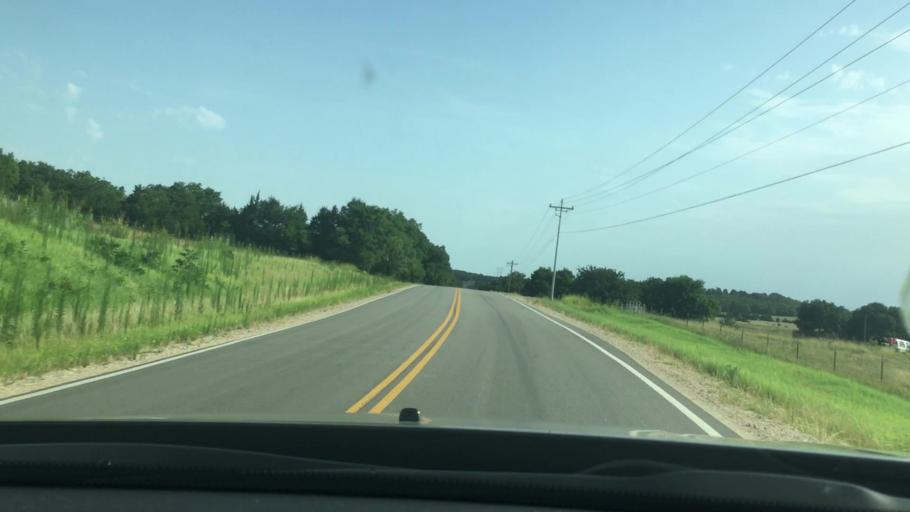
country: US
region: Oklahoma
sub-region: Pontotoc County
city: Byng
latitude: 34.8541
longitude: -96.6135
